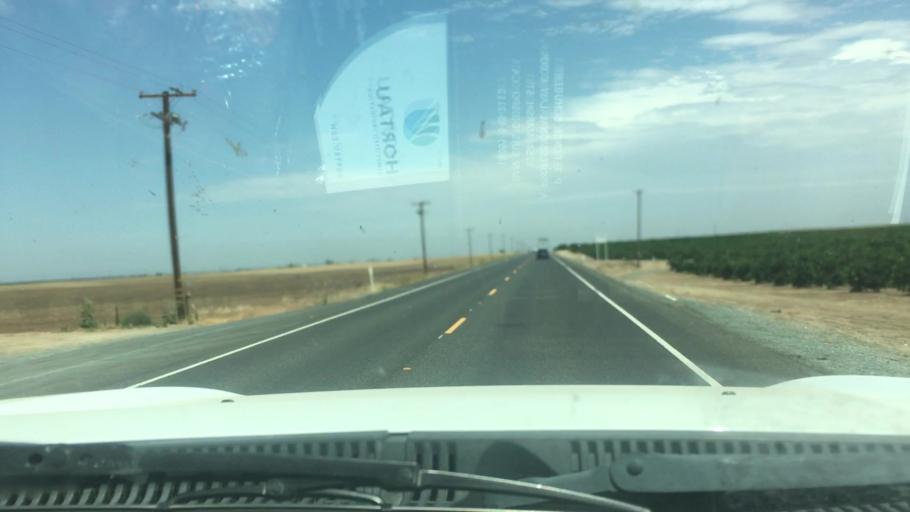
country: US
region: California
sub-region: Tulare County
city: Richgrove
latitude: 35.8184
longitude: -119.0536
